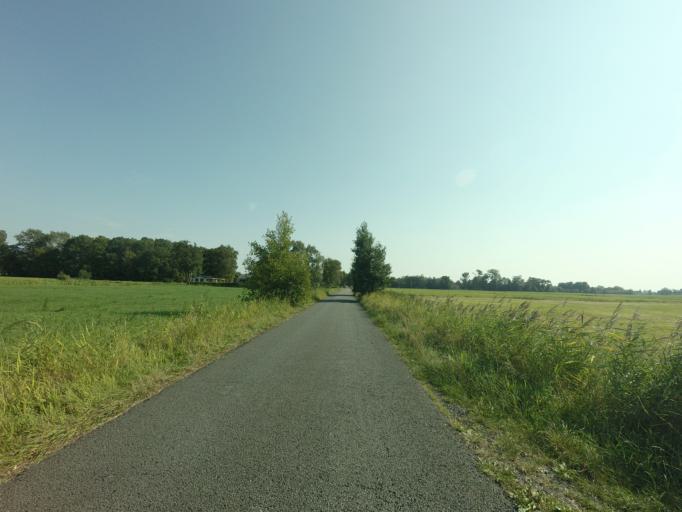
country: NL
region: Groningen
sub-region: Gemeente Zuidhorn
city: Zuidhorn
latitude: 53.2063
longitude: 6.4373
